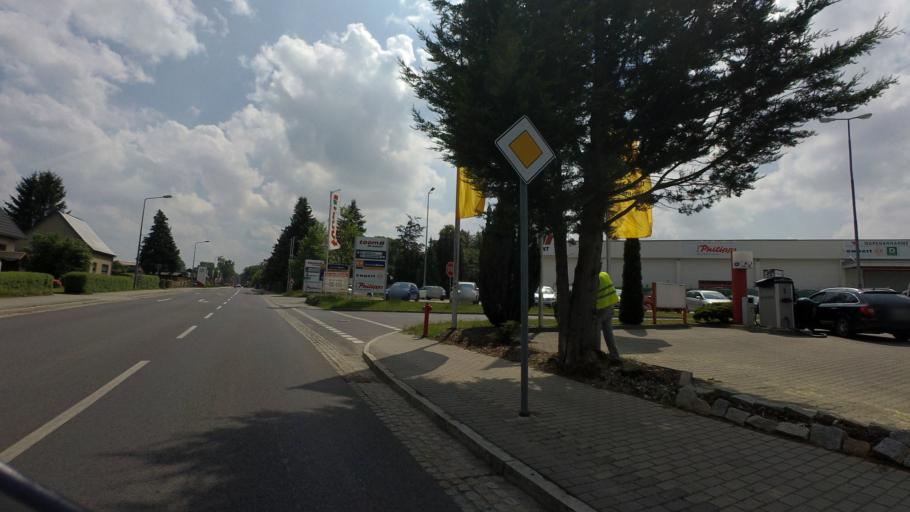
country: DE
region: Saxony
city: Weisswasser
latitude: 51.5126
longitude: 14.6126
